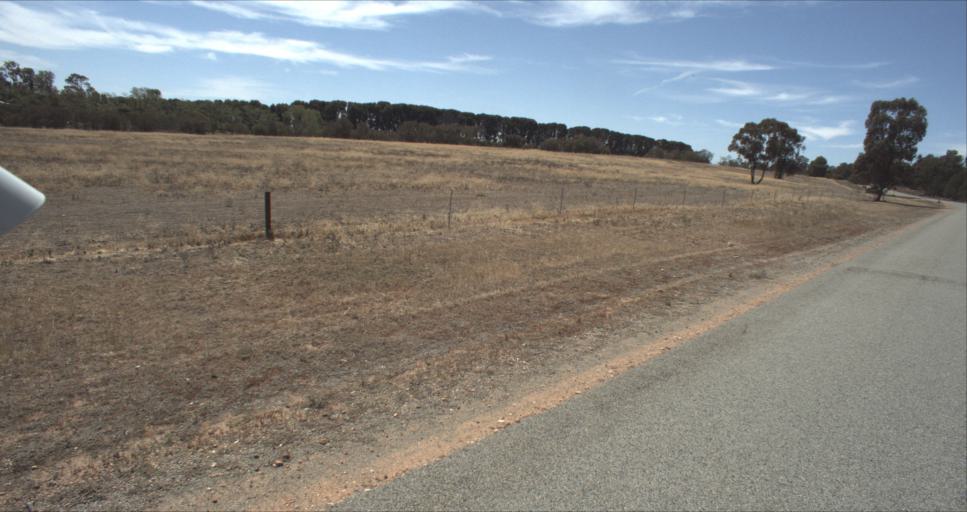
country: AU
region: New South Wales
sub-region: Leeton
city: Leeton
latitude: -34.6716
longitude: 146.4404
